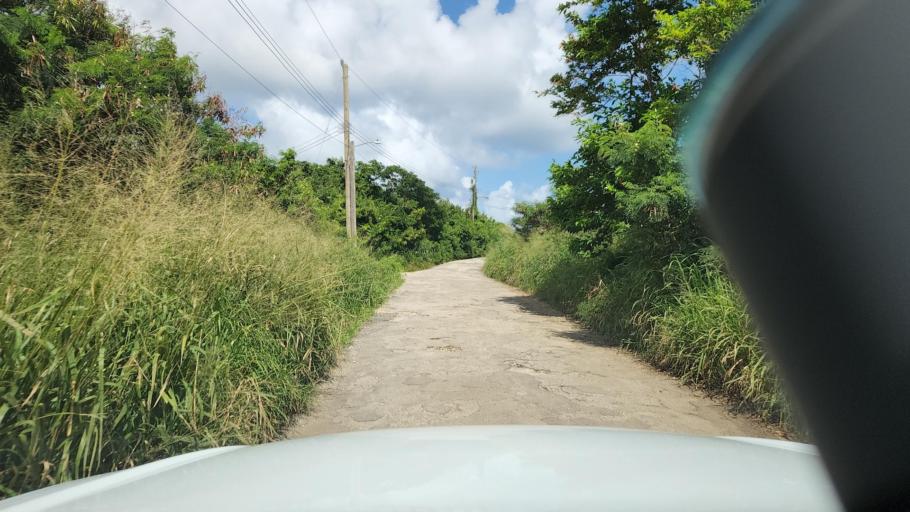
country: BB
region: Saint John
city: Four Cross Roads
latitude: 13.1699
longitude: -59.5016
